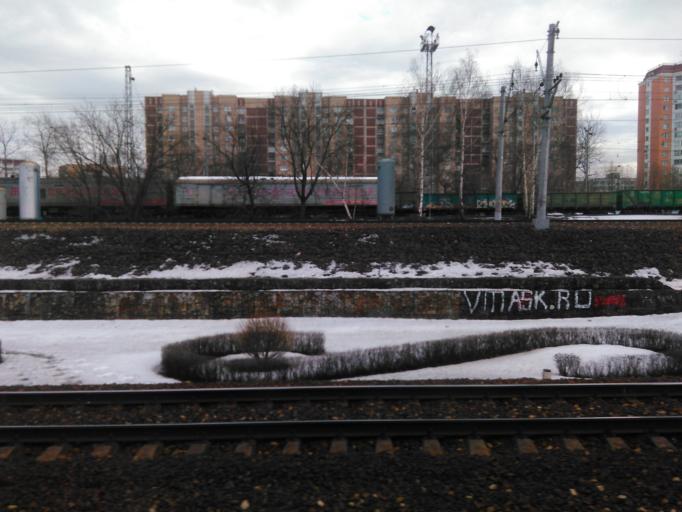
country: RU
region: Moscow
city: Yaroslavskiy
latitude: 55.8779
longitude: 37.7073
